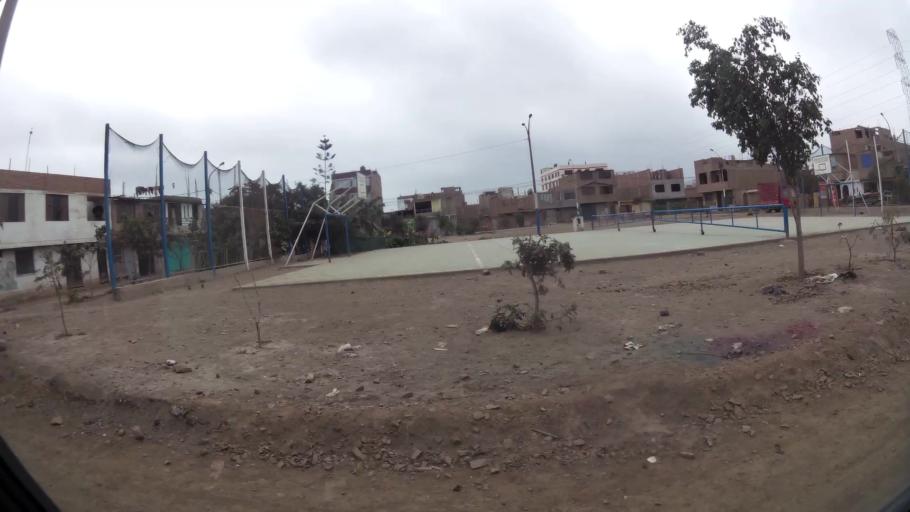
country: PE
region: Lima
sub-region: Lima
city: Independencia
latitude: -11.9699
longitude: -77.0928
